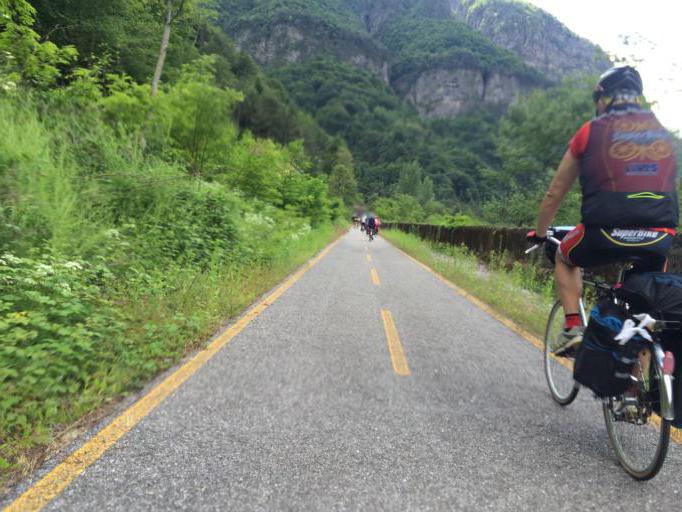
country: IT
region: Friuli Venezia Giulia
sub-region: Provincia di Udine
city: Dogna
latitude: 46.4518
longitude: 13.3172
